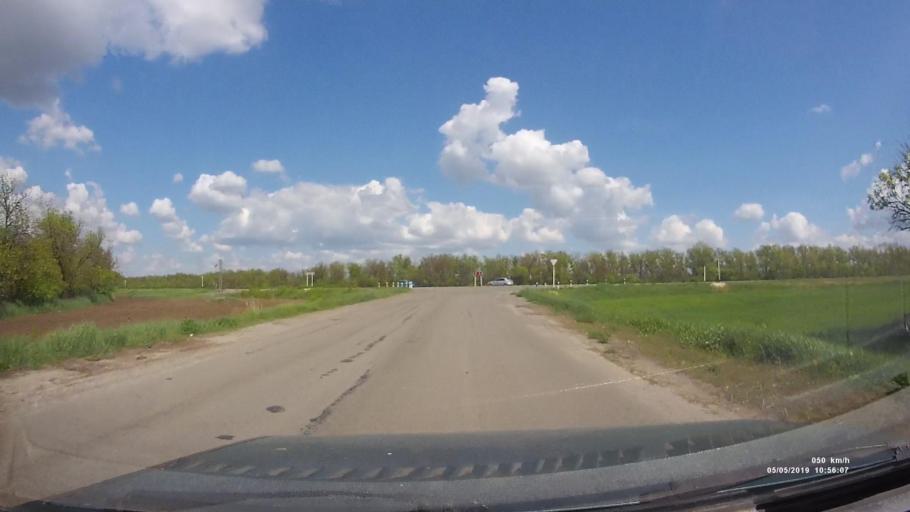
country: RU
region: Rostov
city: Ust'-Donetskiy
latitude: 47.6713
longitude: 40.8204
